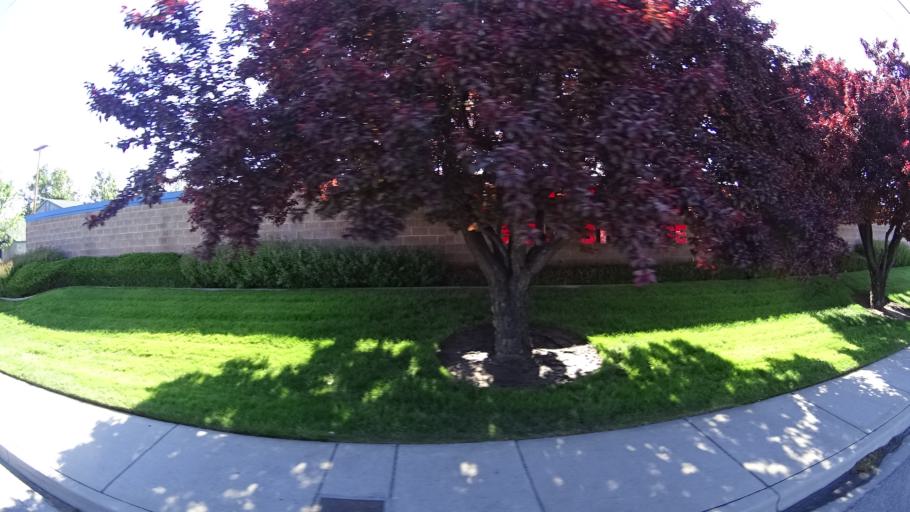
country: US
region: Idaho
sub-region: Ada County
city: Garden City
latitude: 43.5931
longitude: -116.2435
